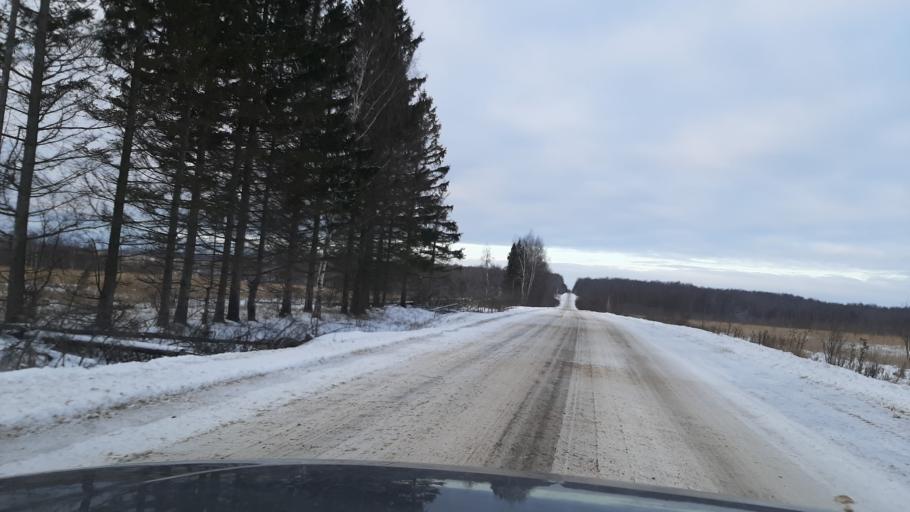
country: RU
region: Kostroma
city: Kosmynino
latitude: 57.4813
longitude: 40.7673
